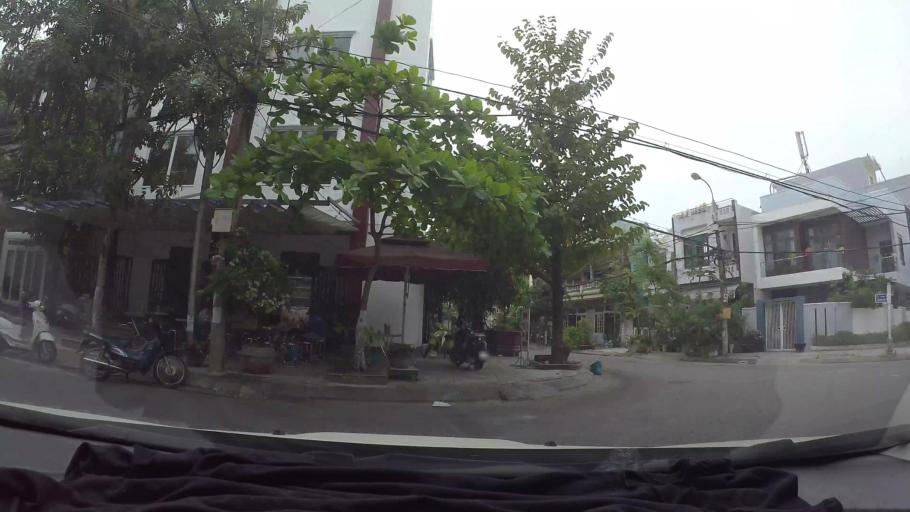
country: VN
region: Da Nang
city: Cam Le
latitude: 16.0302
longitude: 108.2265
